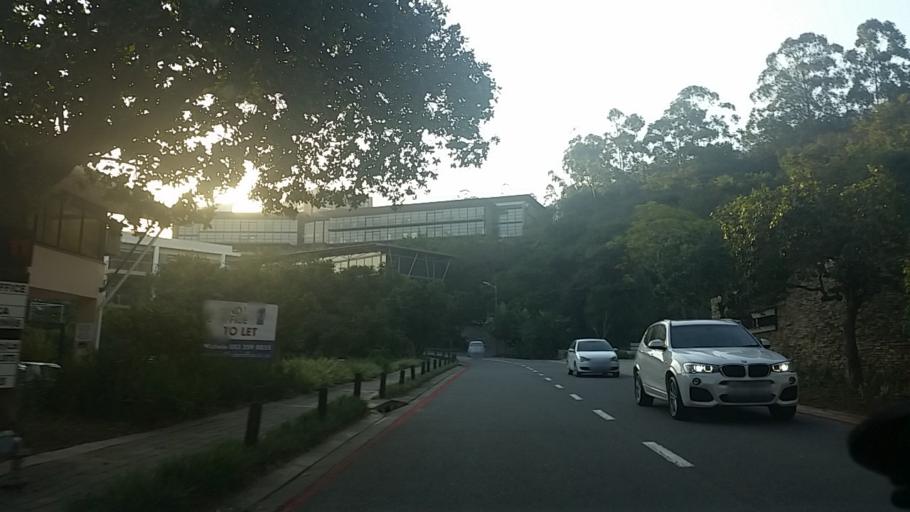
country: ZA
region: KwaZulu-Natal
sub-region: eThekwini Metropolitan Municipality
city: Berea
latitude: -29.8488
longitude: 30.9279
